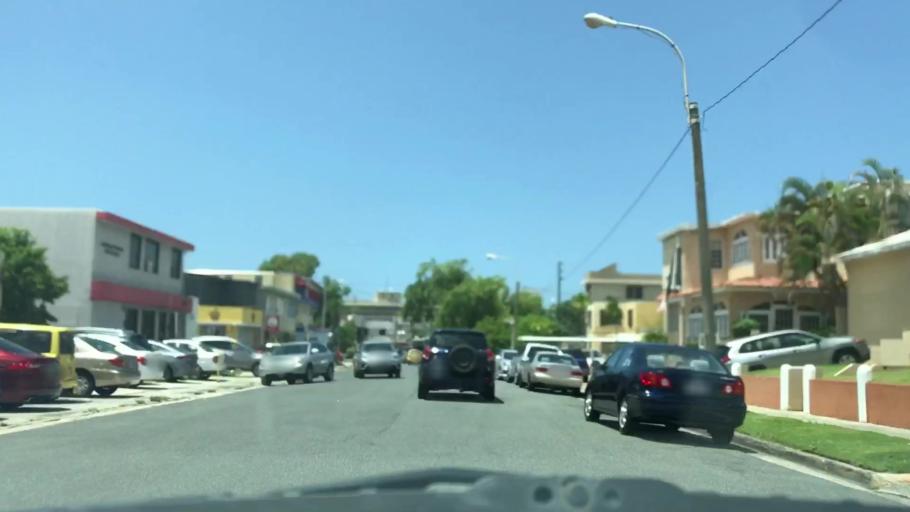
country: PR
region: Catano
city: Catano
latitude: 18.4185
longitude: -66.0624
